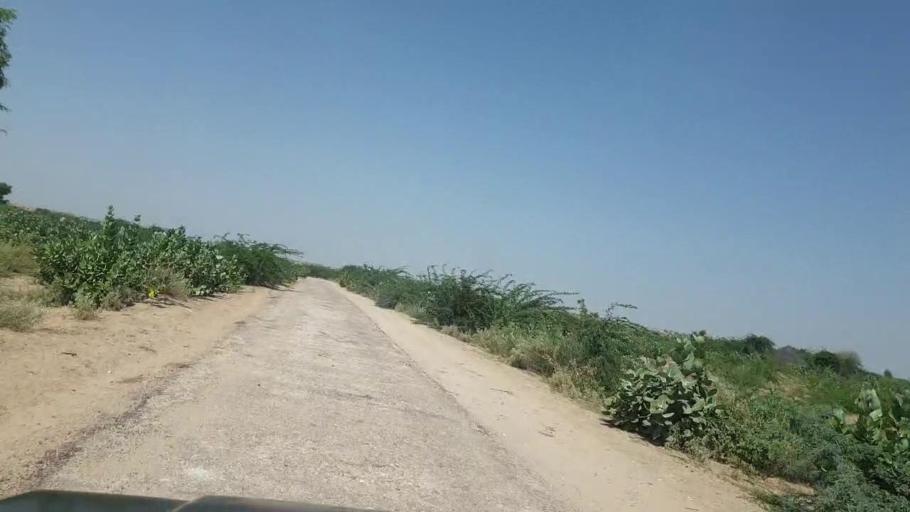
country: PK
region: Sindh
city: Chor
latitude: 25.4015
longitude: 70.3106
